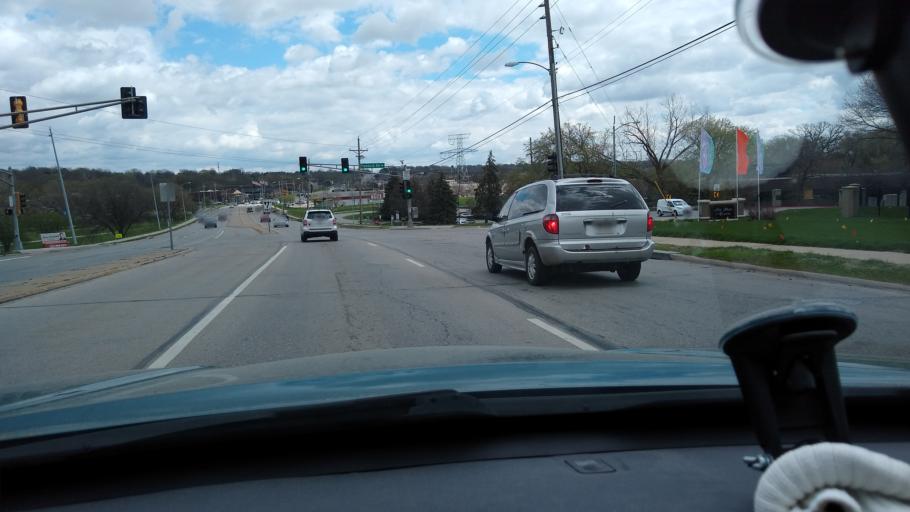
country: US
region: Nebraska
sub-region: Douglas County
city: Ralston
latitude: 41.2334
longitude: -96.0586
